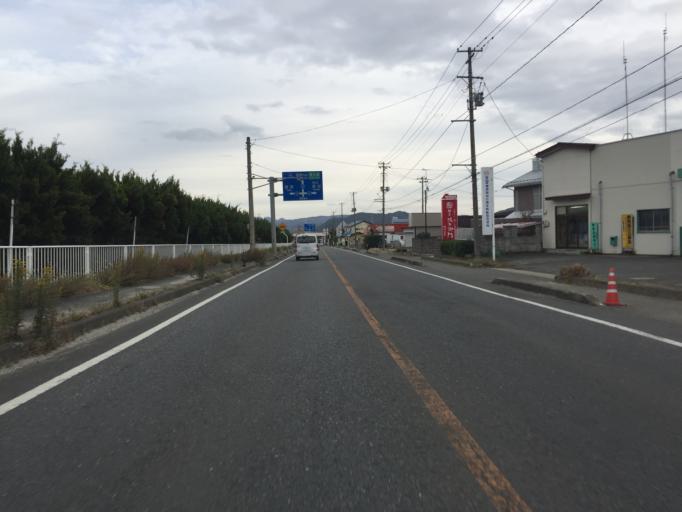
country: JP
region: Fukushima
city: Fukushima-shi
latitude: 37.8134
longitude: 140.4419
